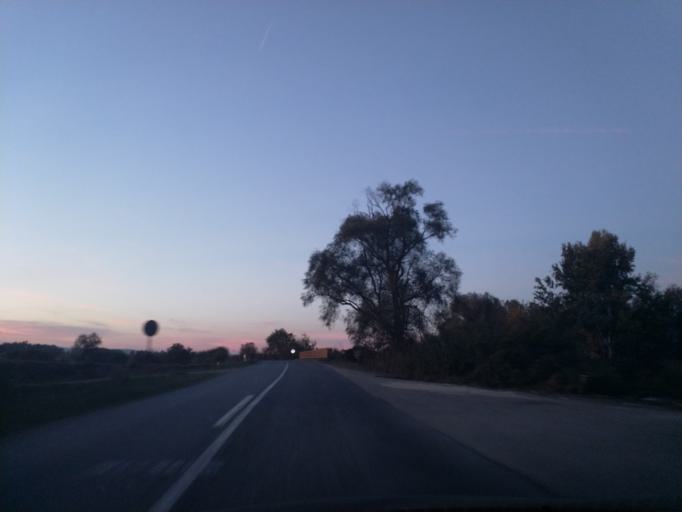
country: RS
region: Central Serbia
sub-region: Pomoravski Okrug
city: Svilajnac
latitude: 44.2285
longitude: 21.1455
